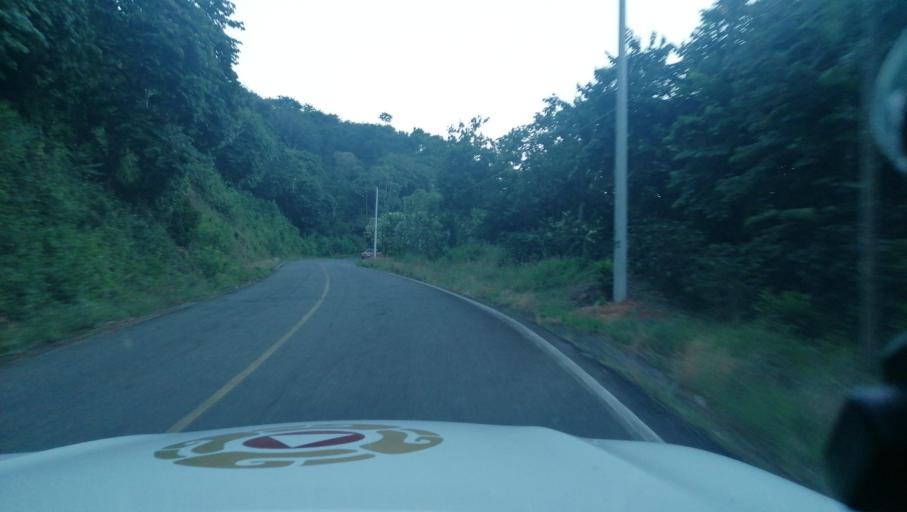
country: MX
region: Chiapas
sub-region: Cacahoatan
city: Benito Juarez
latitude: 15.0385
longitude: -92.2439
